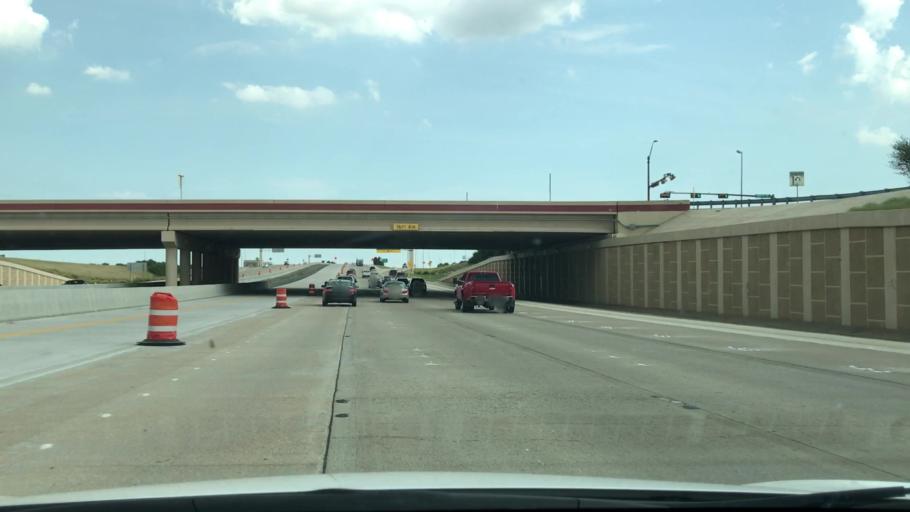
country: US
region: Texas
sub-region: Dallas County
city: Sachse
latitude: 32.9706
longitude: -96.6497
